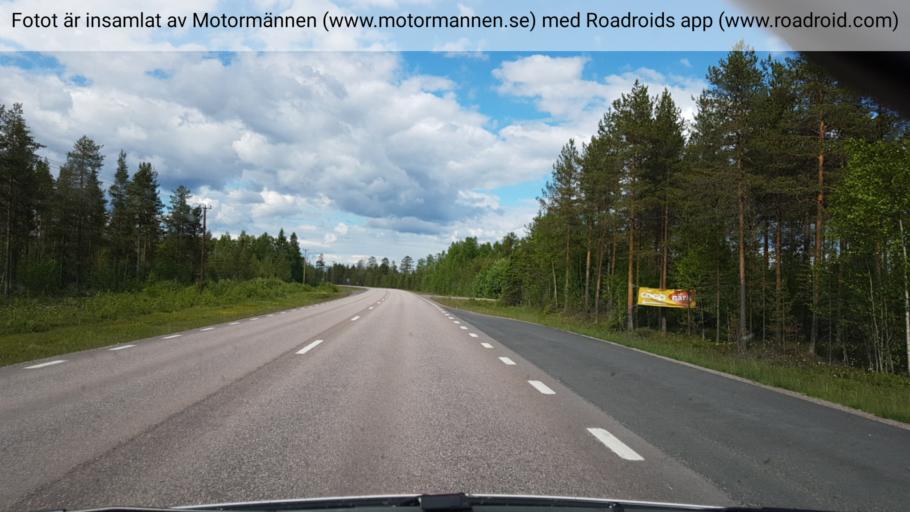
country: SE
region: Norrbotten
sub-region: Kalix Kommun
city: Toere
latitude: 66.0421
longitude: 22.7190
